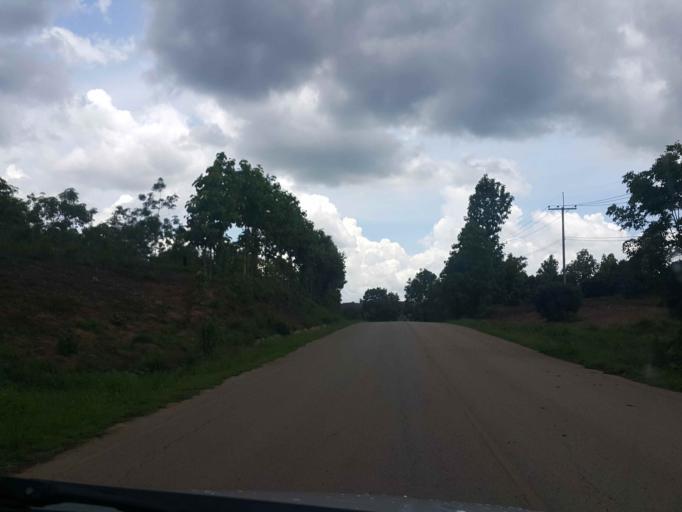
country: TH
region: Phayao
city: Dok Kham Tai
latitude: 18.9713
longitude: 100.0743
